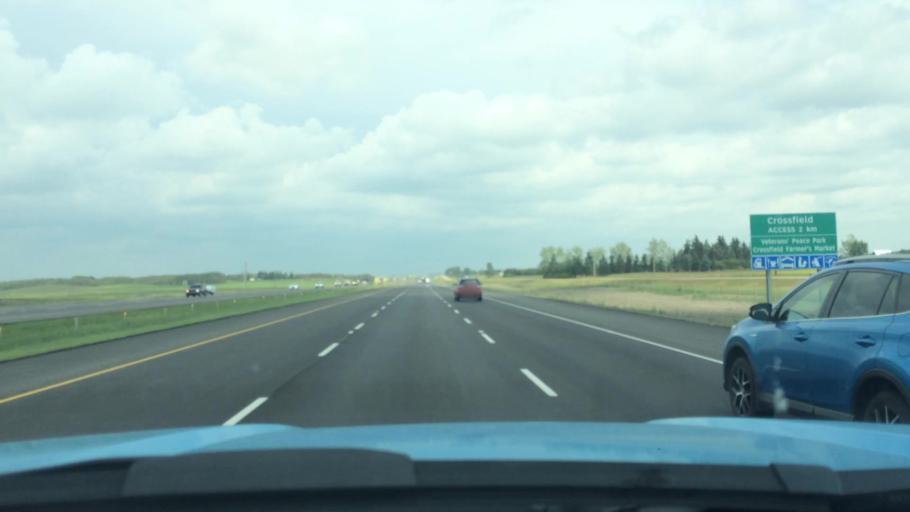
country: CA
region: Alberta
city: Airdrie
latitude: 51.3640
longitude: -114.0016
